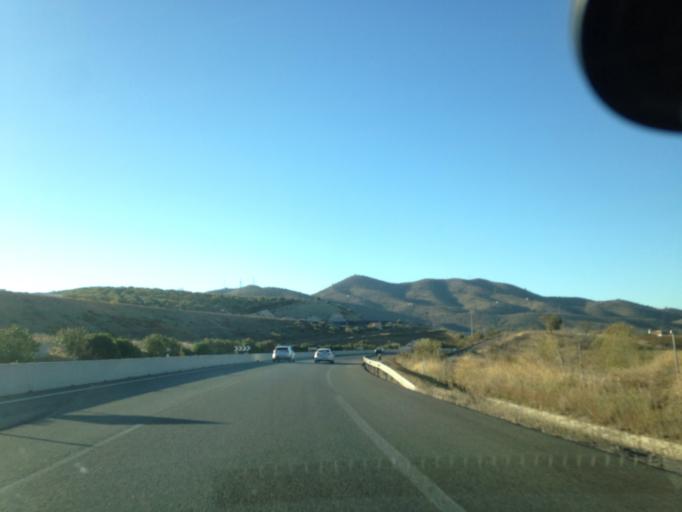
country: ES
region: Andalusia
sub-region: Provincia de Malaga
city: Casabermeja
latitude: 36.9138
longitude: -4.4435
